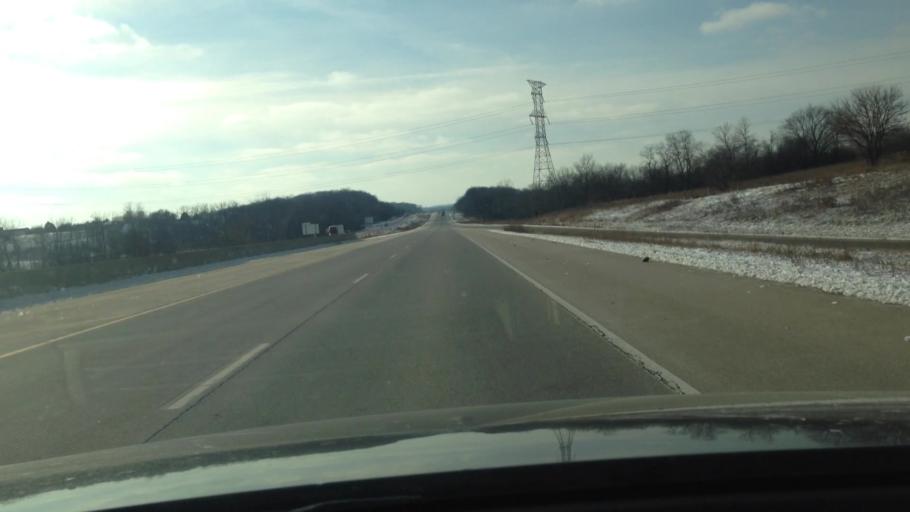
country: US
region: Wisconsin
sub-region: Waukesha County
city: Big Bend
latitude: 42.9086
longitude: -88.2179
